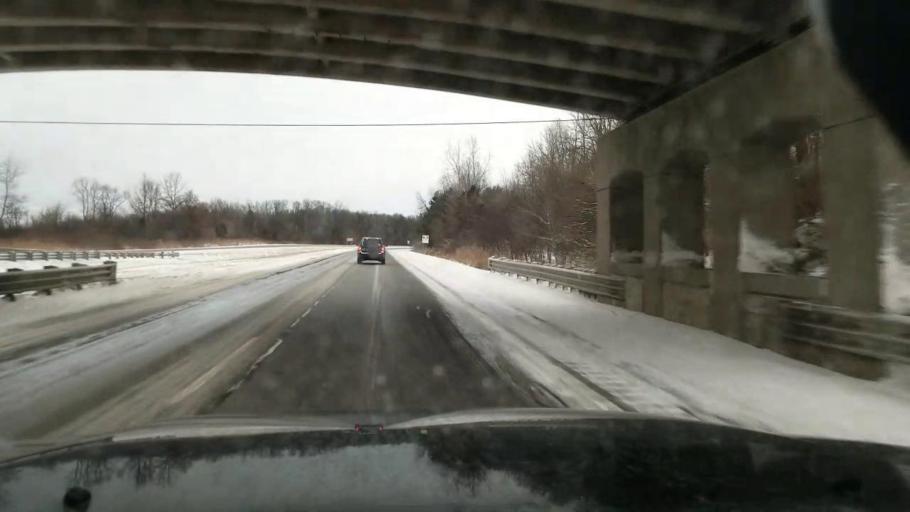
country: US
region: Michigan
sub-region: Jackson County
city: Jackson
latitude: 42.2329
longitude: -84.4753
